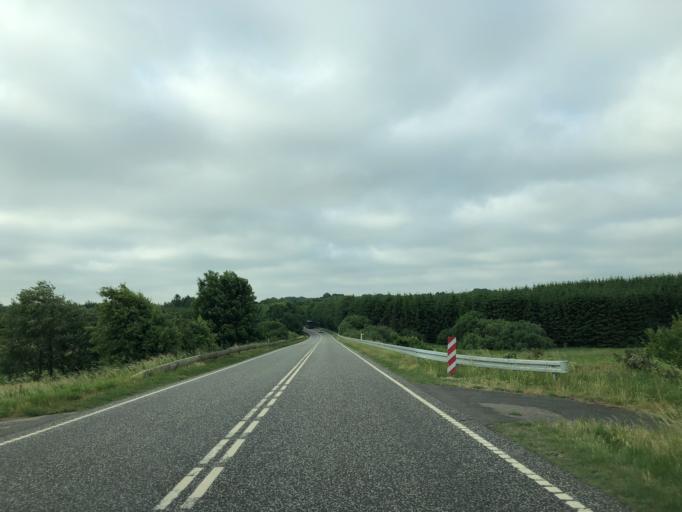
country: DK
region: South Denmark
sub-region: Vejle Kommune
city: Give
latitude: 55.7892
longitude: 9.2733
